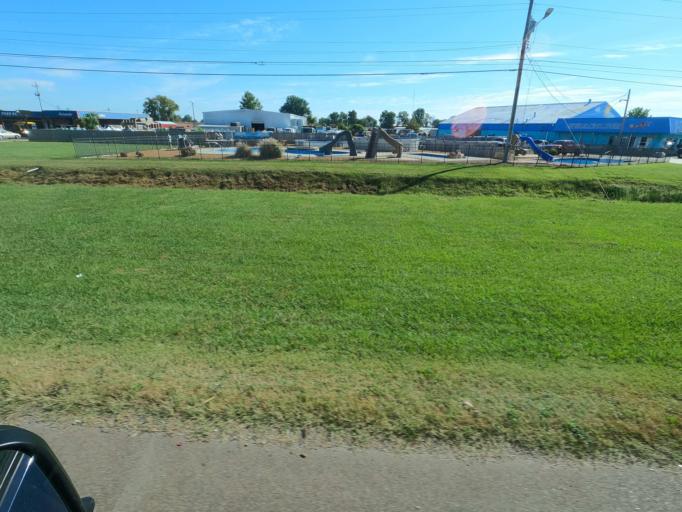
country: US
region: Tennessee
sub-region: Obion County
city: Union City
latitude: 36.4149
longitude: -89.0739
